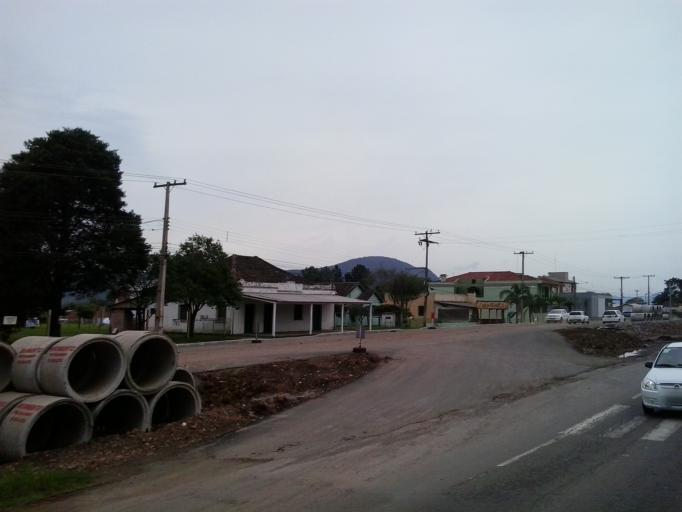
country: BR
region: Rio Grande do Sul
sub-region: Santa Maria
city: Santa Maria
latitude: -29.6942
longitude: -53.7566
